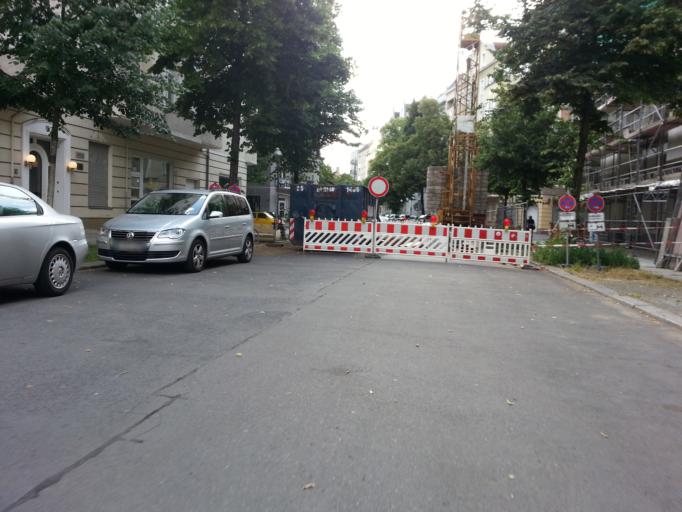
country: DE
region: Berlin
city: Charlottenburg-Nord
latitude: 52.5202
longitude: 13.3029
